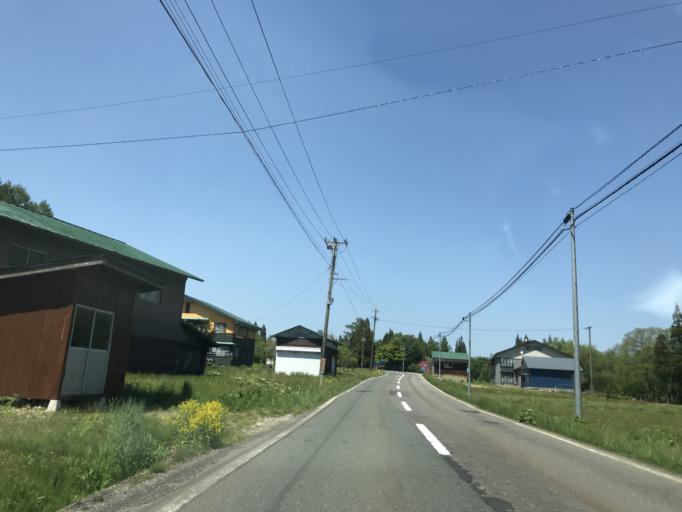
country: JP
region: Iwate
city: Shizukuishi
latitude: 39.5325
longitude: 140.8333
